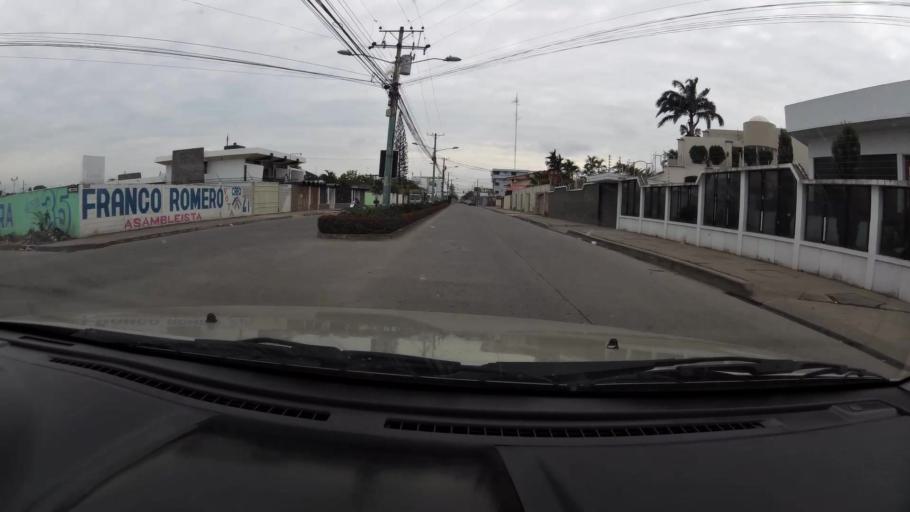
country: EC
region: El Oro
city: Machala
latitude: -3.2493
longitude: -79.9571
